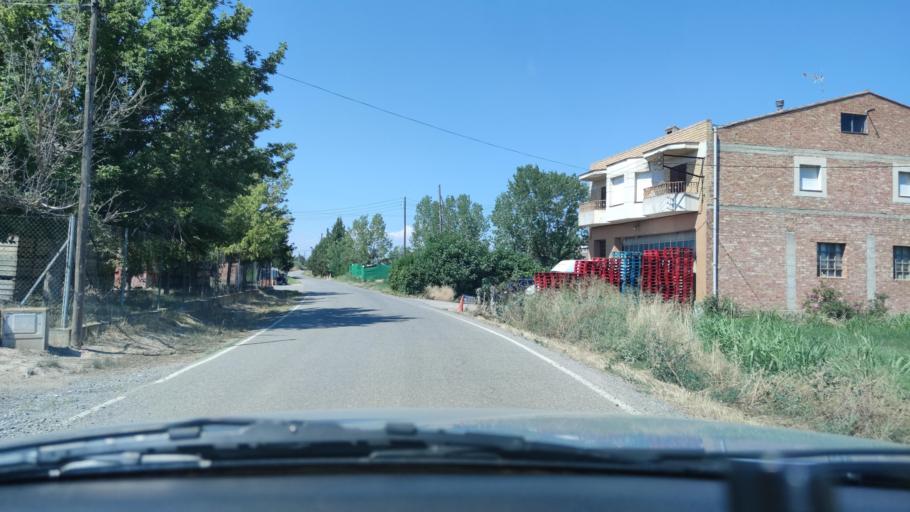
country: ES
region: Catalonia
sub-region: Provincia de Lleida
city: Lleida
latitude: 41.6454
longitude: 0.6227
